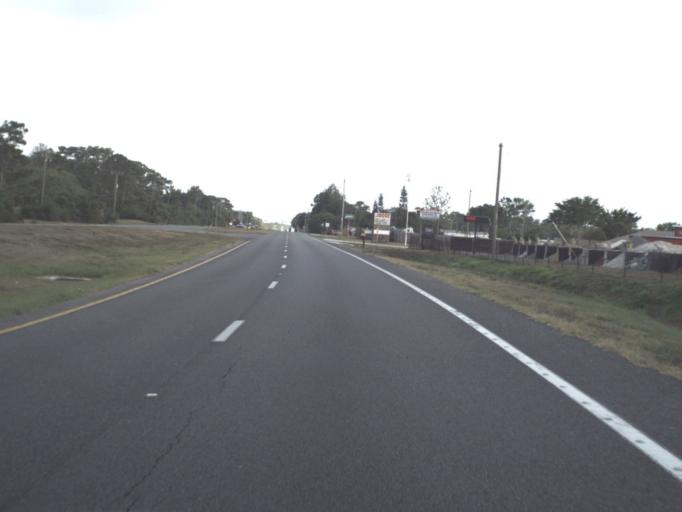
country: US
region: Florida
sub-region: Brevard County
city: Mims
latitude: 28.6922
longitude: -80.8577
